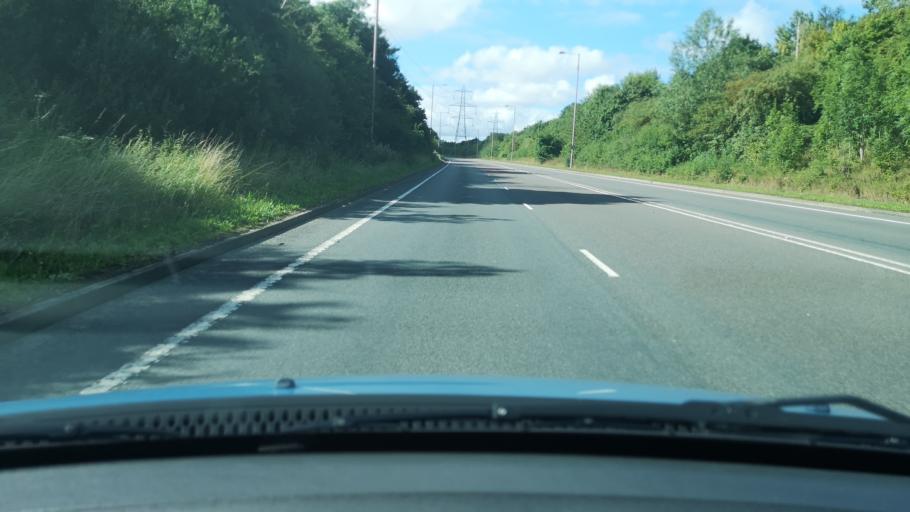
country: GB
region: England
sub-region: City and Borough of Wakefield
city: Normanton
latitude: 53.6900
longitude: -1.4041
